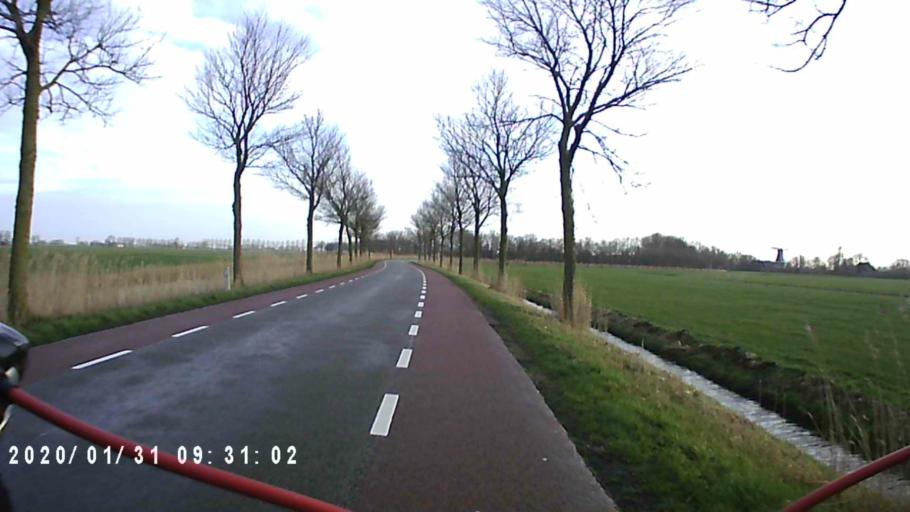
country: NL
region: Groningen
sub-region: Gemeente Zuidhorn
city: Aduard
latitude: 53.3048
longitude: 6.4582
